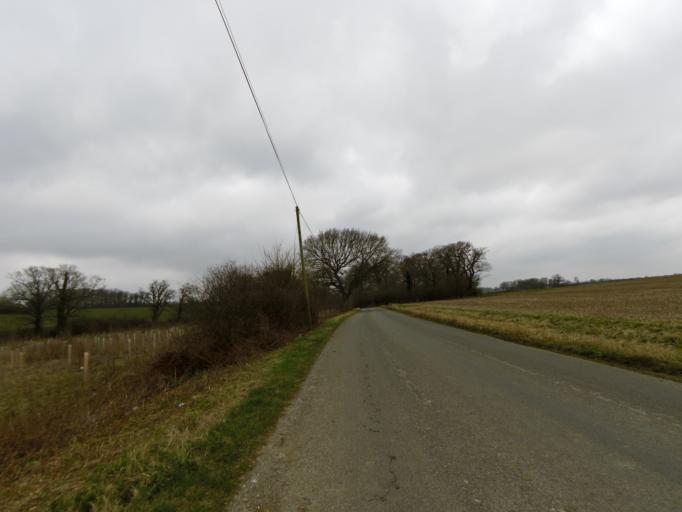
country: GB
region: England
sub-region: Suffolk
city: Cookley
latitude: 52.2874
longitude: 1.4628
